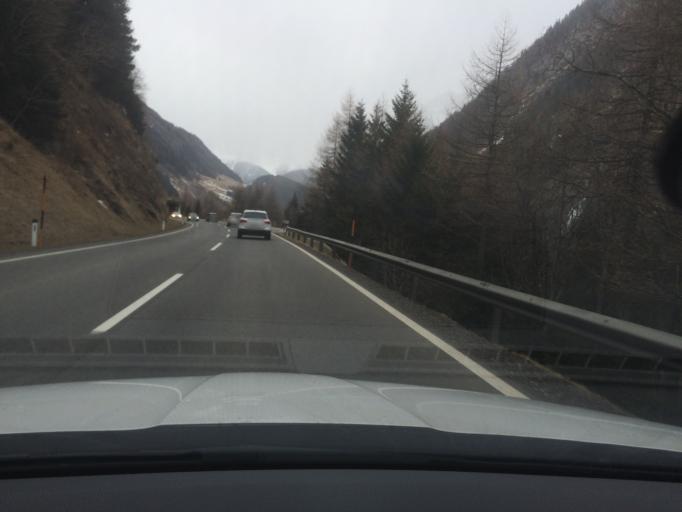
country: AT
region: Tyrol
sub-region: Politischer Bezirk Lienz
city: Matrei in Osttirol
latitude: 47.0793
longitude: 12.5309
